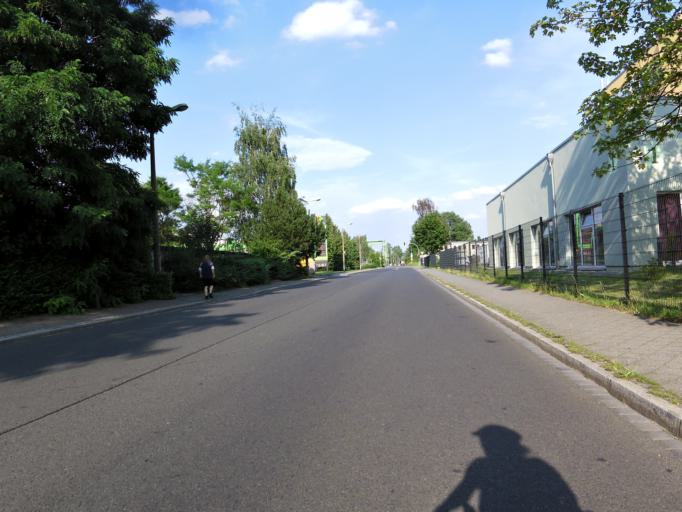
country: DE
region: Saxony
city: Taucha
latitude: 51.3587
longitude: 12.4285
